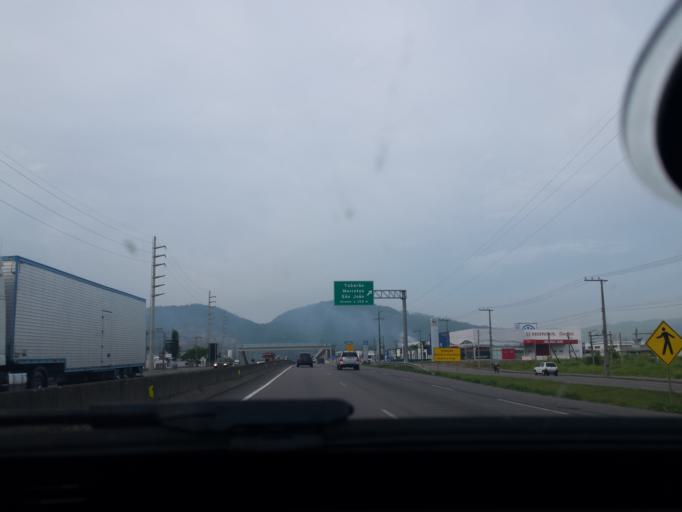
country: BR
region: Santa Catarina
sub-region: Tubarao
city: Tubarao
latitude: -28.4723
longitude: -49.0230
